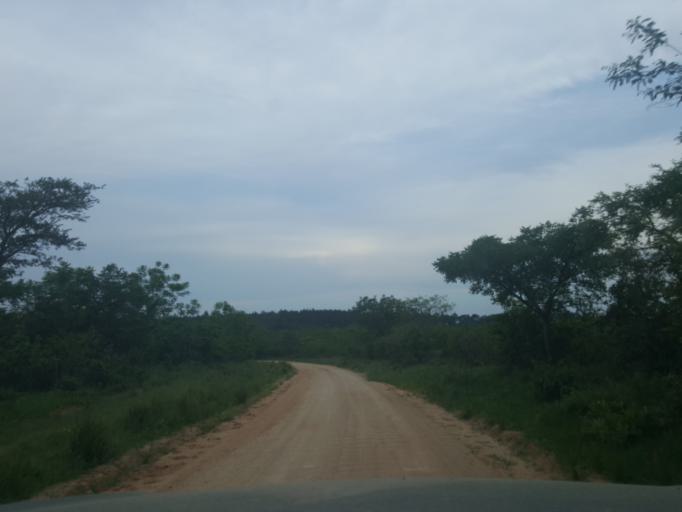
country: ZA
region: Limpopo
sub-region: Mopani District Municipality
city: Hoedspruit
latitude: -24.5958
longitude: 30.9311
